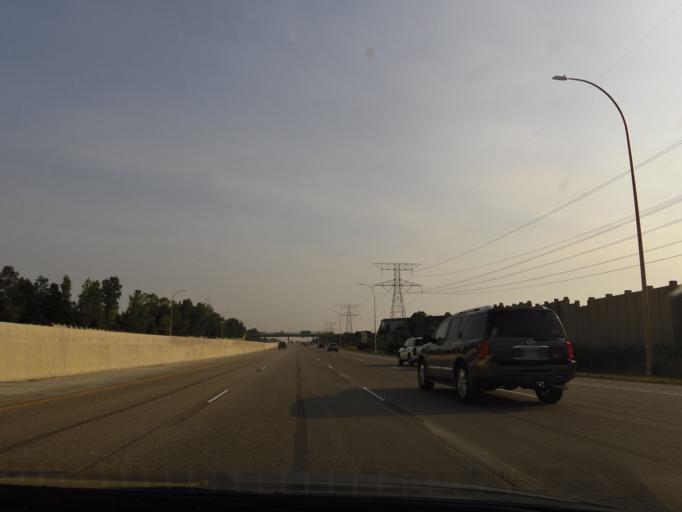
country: US
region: Minnesota
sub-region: Hennepin County
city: Maple Grove
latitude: 45.0846
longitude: -93.4472
